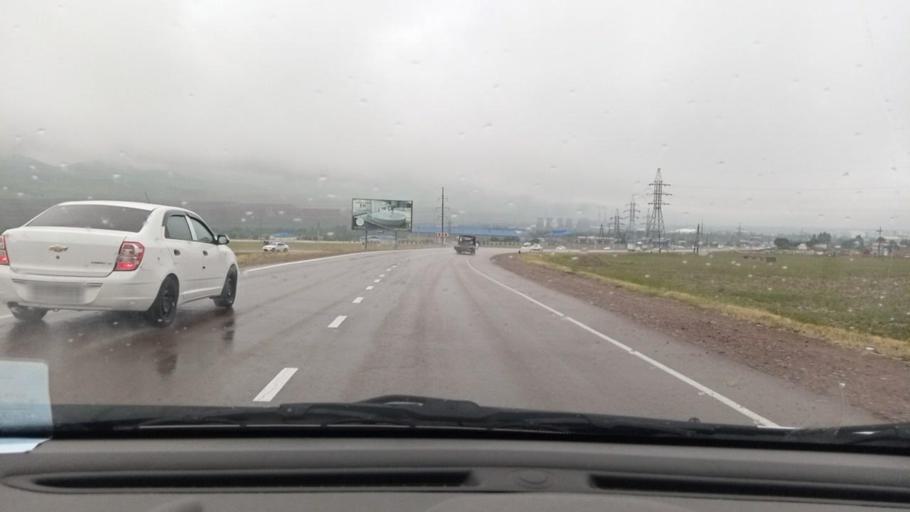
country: UZ
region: Toshkent
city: Angren
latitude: 41.0364
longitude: 70.1437
